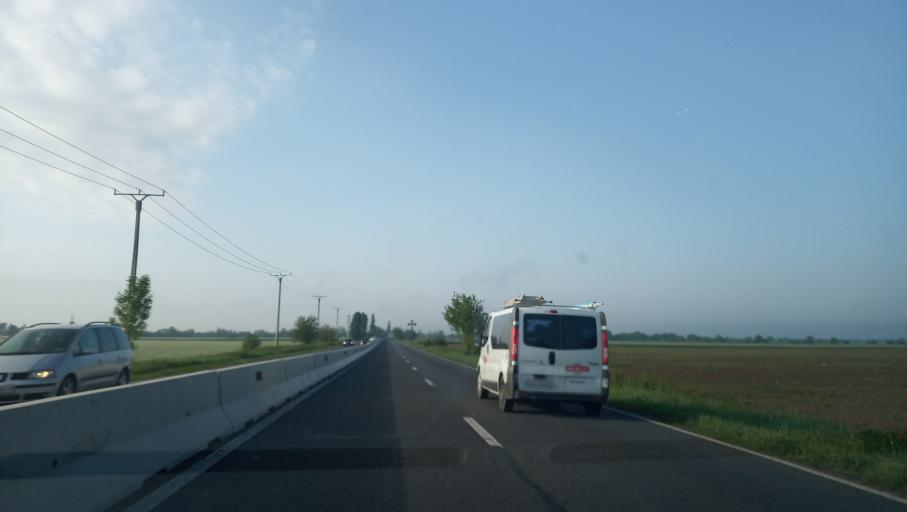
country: RO
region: Timis
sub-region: Comuna Sag
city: Sag
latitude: 45.6744
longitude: 21.1706
